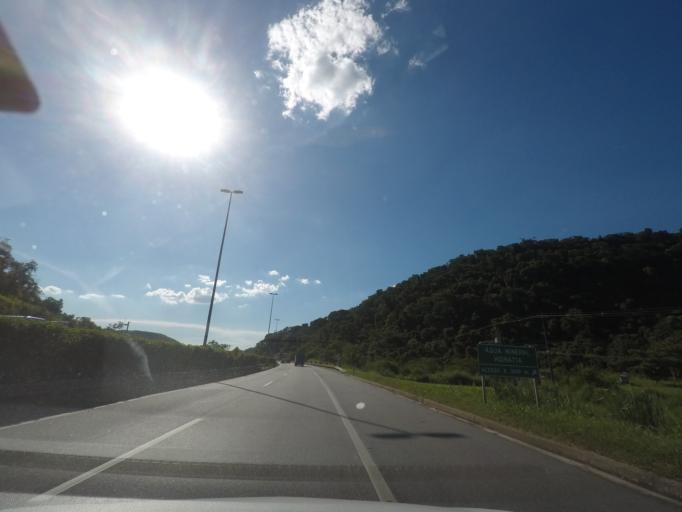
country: BR
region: Rio de Janeiro
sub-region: Petropolis
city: Petropolis
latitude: -22.6541
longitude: -43.1438
